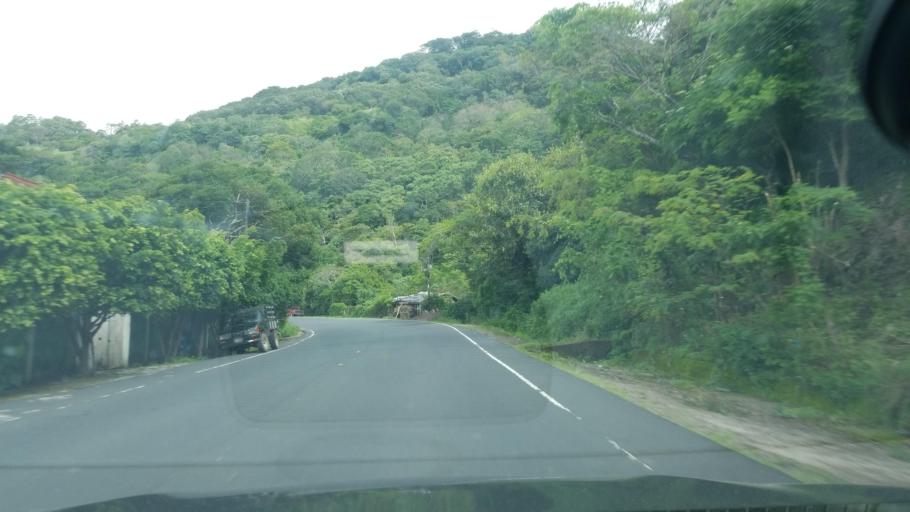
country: HN
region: Choluteca
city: Corpus
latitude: 13.3732
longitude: -86.9456
